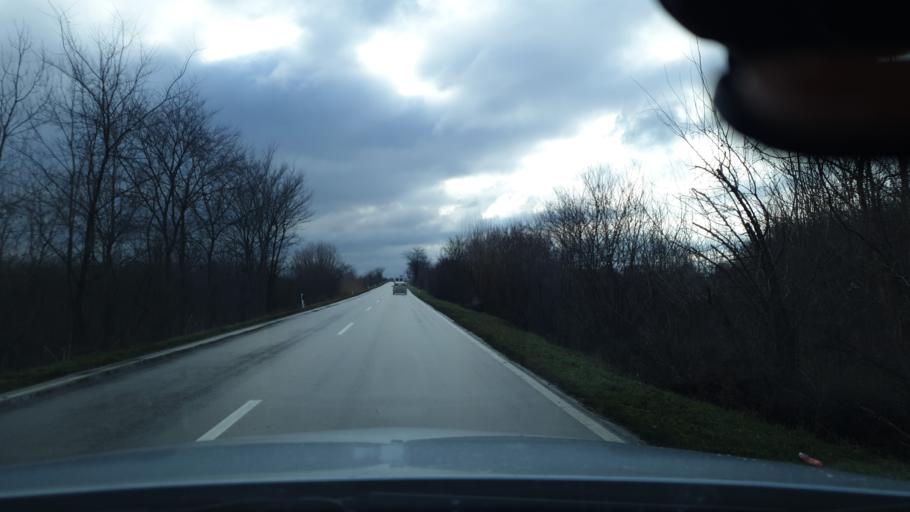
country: RS
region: Central Serbia
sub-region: Branicevski Okrug
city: Malo Crnice
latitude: 44.4942
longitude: 21.3275
